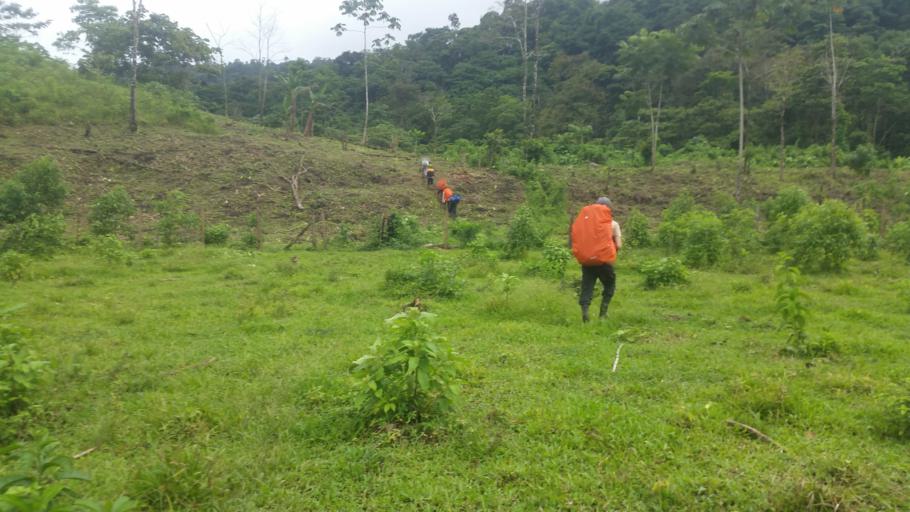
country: NI
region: Atlantico Norte (RAAN)
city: Bonanza
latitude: 14.0267
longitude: -84.7259
